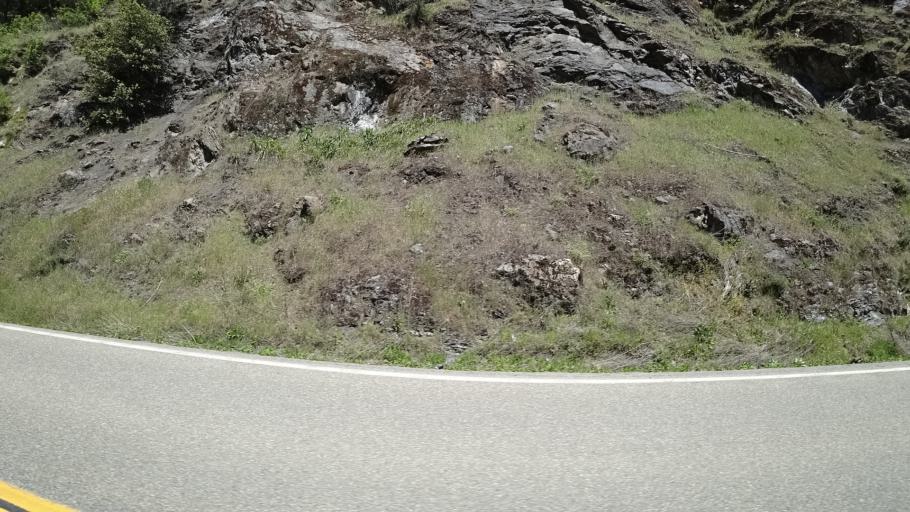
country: US
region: California
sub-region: Trinity County
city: Hayfork
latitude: 40.7716
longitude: -123.3087
